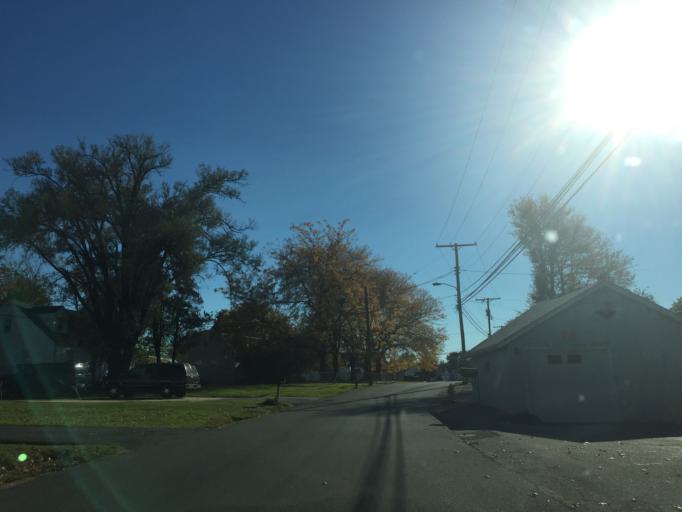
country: US
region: Maryland
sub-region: Baltimore County
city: Edgemere
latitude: 39.2684
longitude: -76.4768
